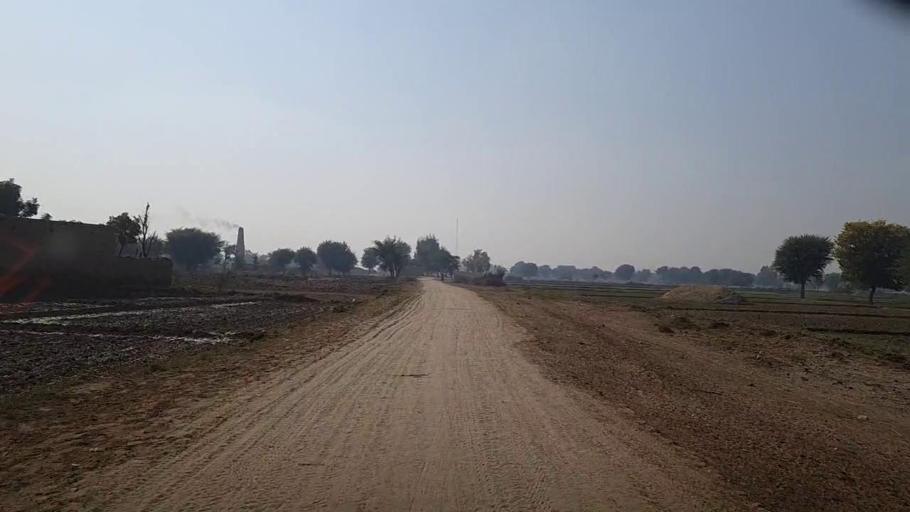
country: PK
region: Sindh
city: Bozdar
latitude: 27.2135
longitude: 68.5772
